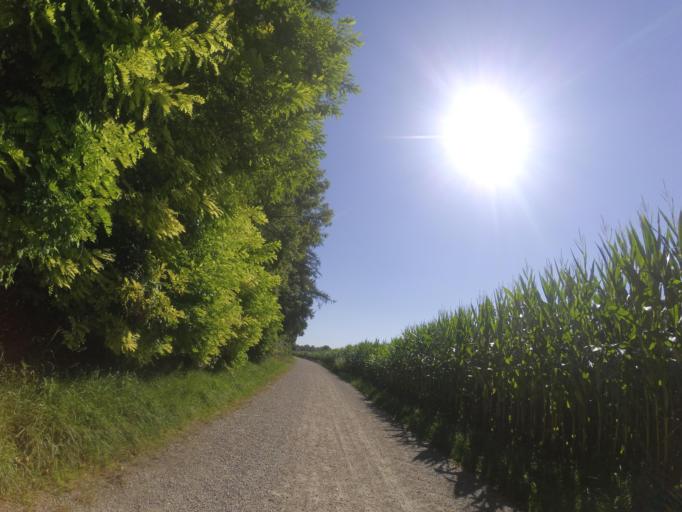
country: DE
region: Bavaria
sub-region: Swabia
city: Nersingen
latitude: 48.4504
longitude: 10.0696
